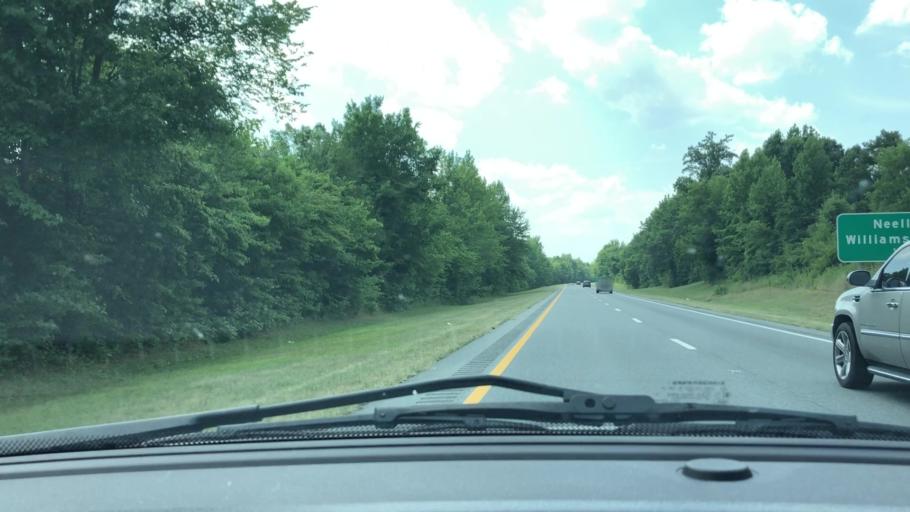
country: US
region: North Carolina
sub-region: Guilford County
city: Forest Oaks
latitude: 35.9749
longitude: -79.7259
